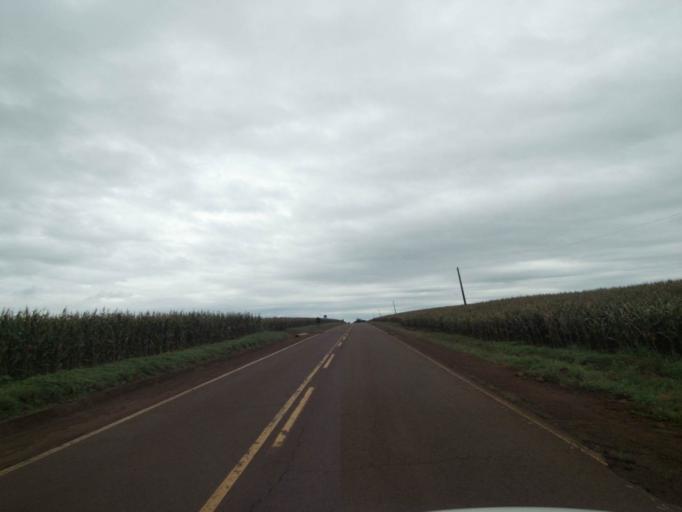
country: BR
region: Parana
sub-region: Marechal Candido Rondon
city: Marechal Candido Rondon
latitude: -24.8002
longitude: -54.2051
